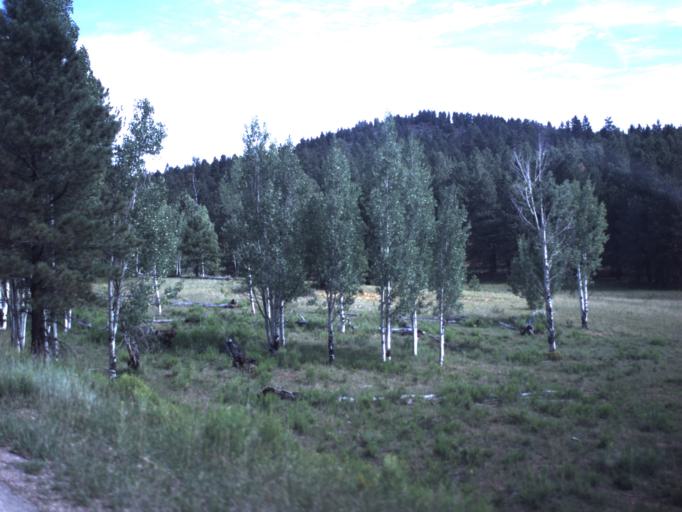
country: US
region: Utah
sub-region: Garfield County
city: Panguitch
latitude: 37.5074
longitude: -112.6276
